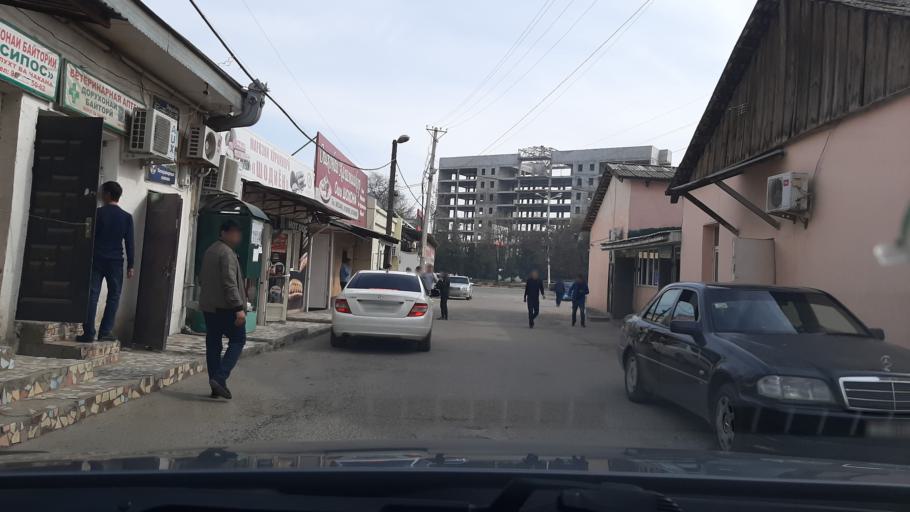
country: TJ
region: Dushanbe
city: Dushanbe
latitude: 38.5624
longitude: 68.7752
